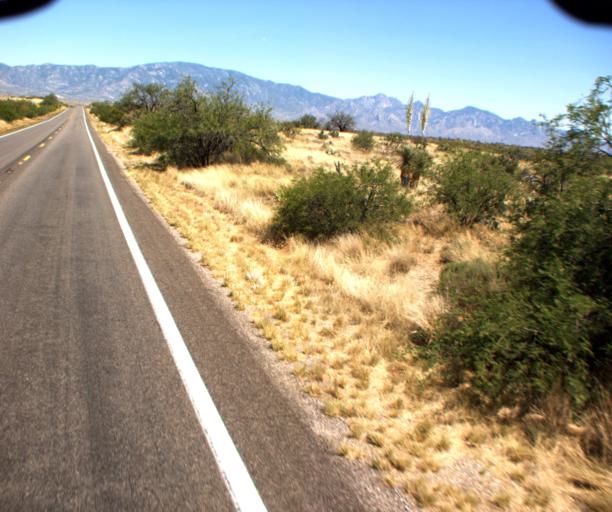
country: US
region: Arizona
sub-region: Pima County
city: Catalina
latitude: 32.5898
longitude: -110.9673
